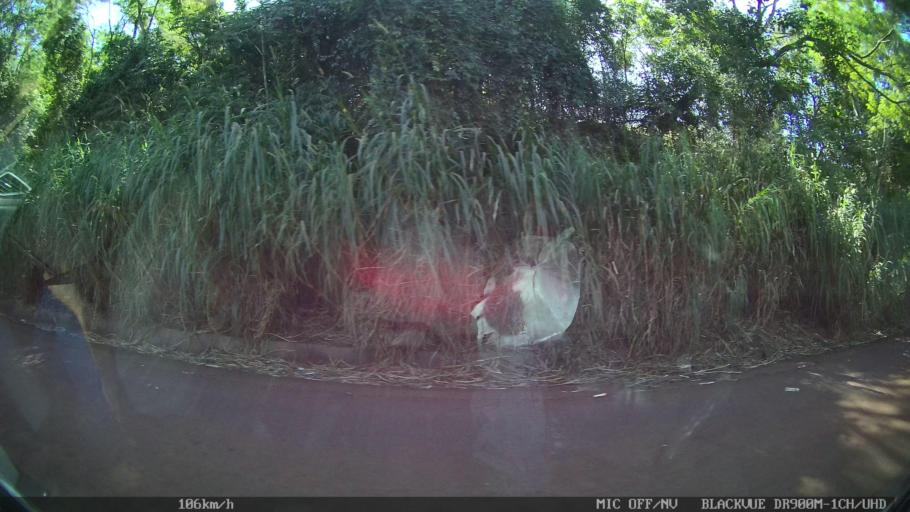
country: BR
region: Sao Paulo
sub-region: Sao Joaquim Da Barra
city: Sao Joaquim da Barra
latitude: -20.5533
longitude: -47.6667
